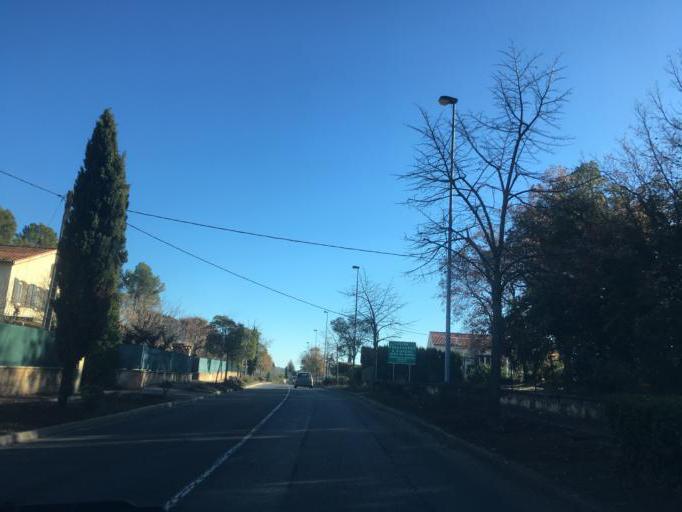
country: FR
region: Provence-Alpes-Cote d'Azur
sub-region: Departement du Var
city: Flayosc
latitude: 43.5384
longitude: 6.3837
